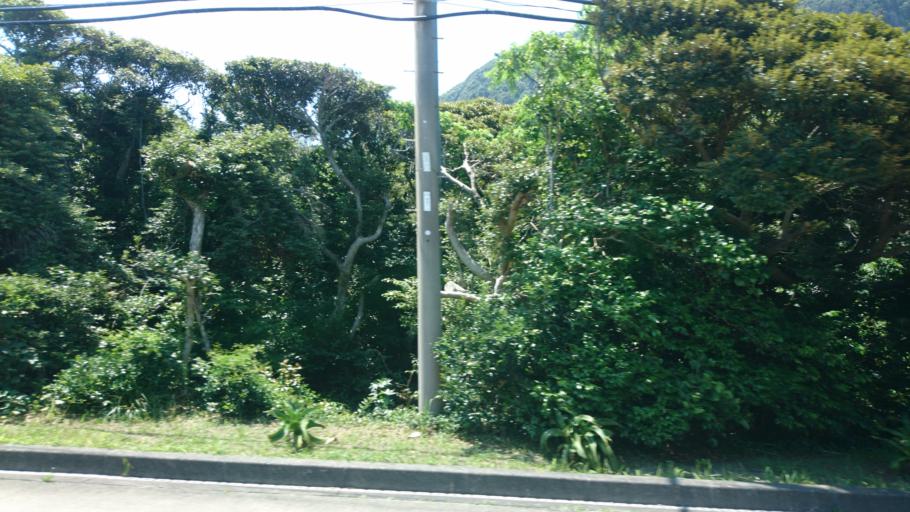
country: JP
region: Shizuoka
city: Shimoda
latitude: 34.3820
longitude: 139.2735
